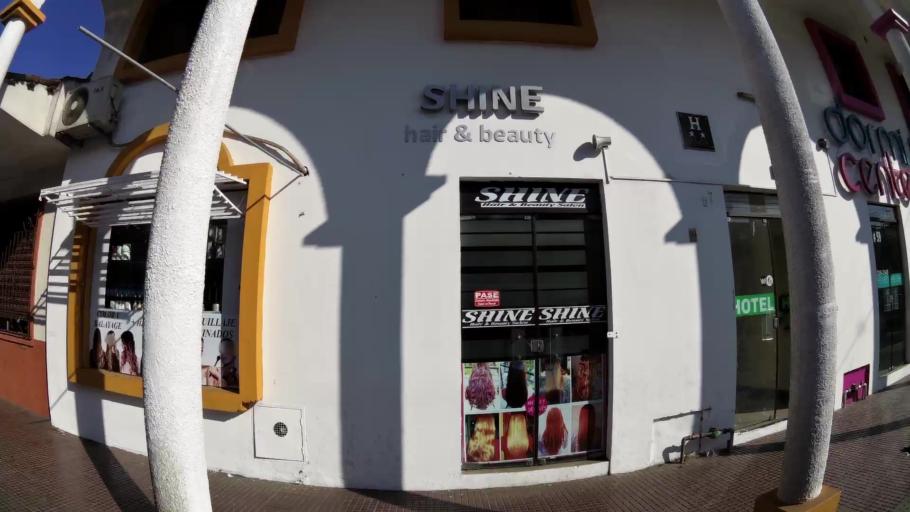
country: BO
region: Santa Cruz
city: Santa Cruz de la Sierra
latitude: -17.7807
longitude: -63.1824
